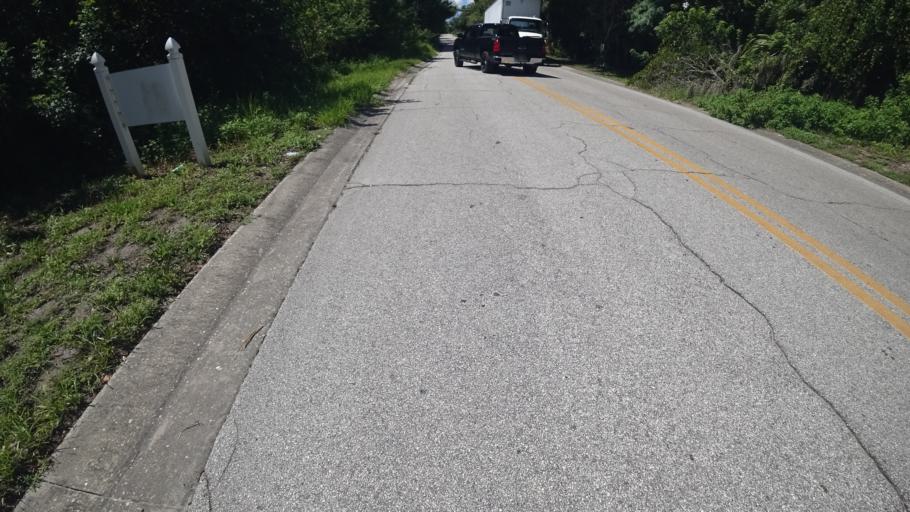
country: US
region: Florida
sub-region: Manatee County
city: Whitfield
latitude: 27.4110
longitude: -82.5306
